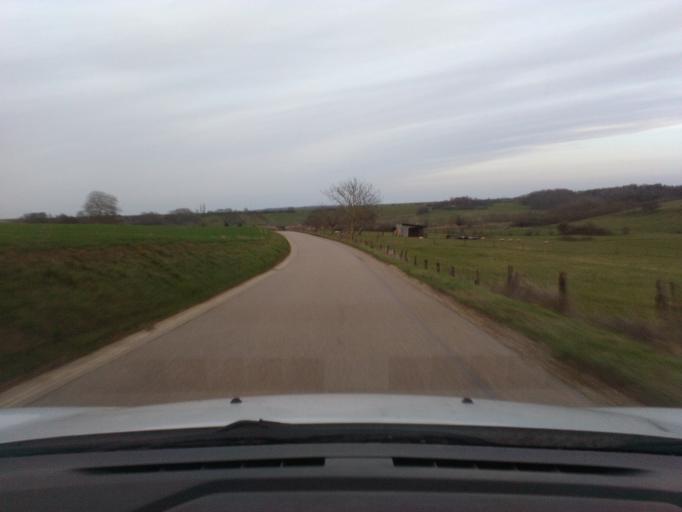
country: FR
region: Lorraine
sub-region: Departement des Vosges
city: Mirecourt
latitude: 48.3036
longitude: 6.0972
